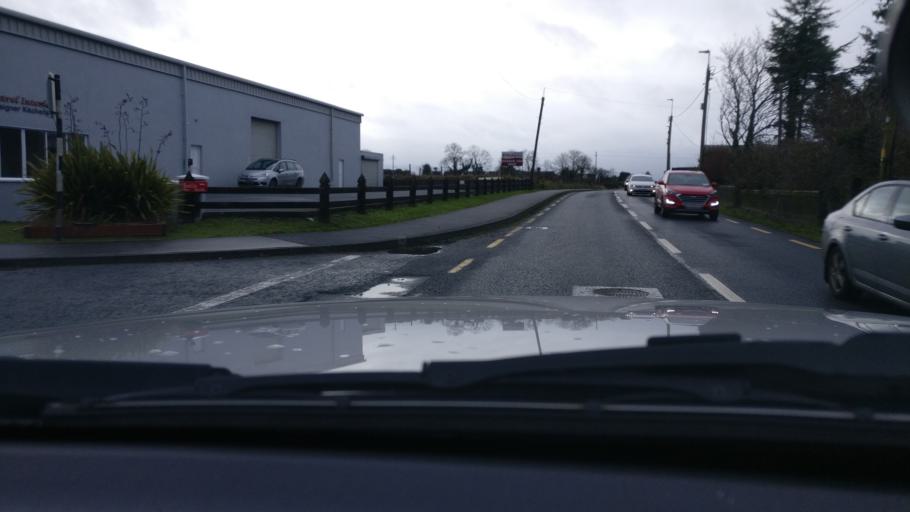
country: IE
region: Leinster
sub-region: An Longfort
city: Ballymahon
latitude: 53.5589
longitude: -7.7648
